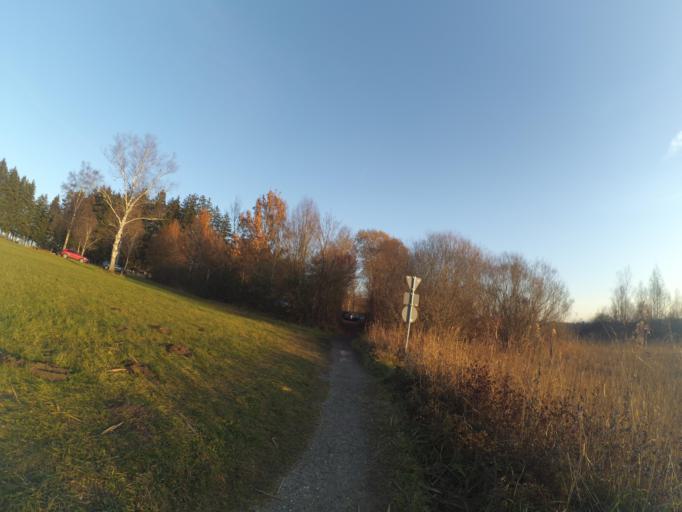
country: DE
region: Bavaria
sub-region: Swabia
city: Aitrang
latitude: 47.8039
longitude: 10.5488
